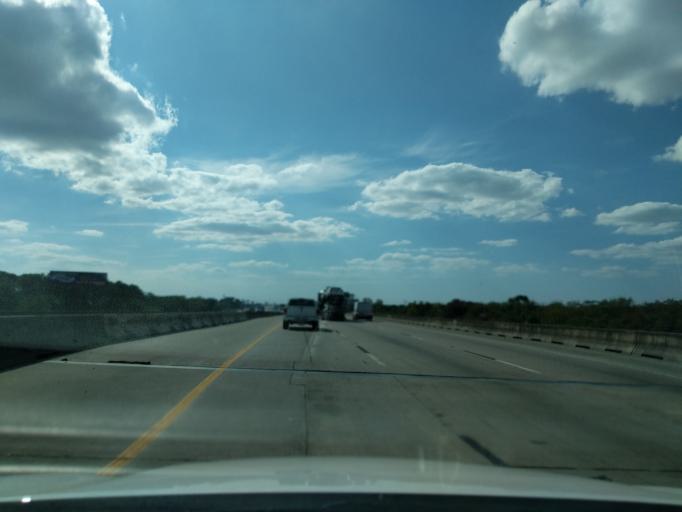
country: US
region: Texas
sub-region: Harris County
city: Baytown
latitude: 29.8081
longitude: -94.9655
